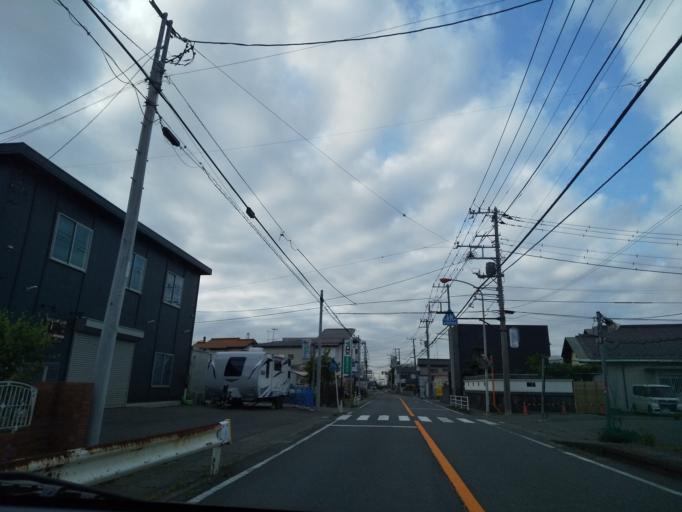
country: JP
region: Kanagawa
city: Zama
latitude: 35.5403
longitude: 139.3669
